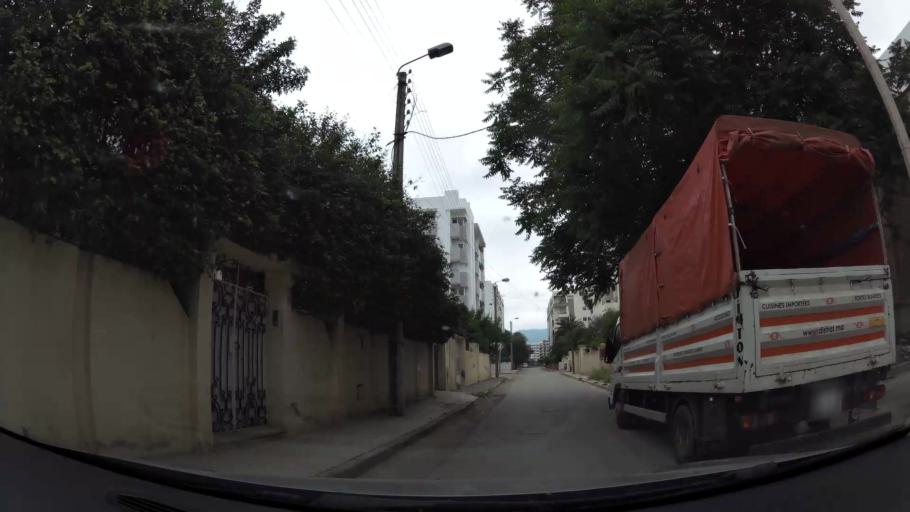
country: MA
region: Fes-Boulemane
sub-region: Fes
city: Fes
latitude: 34.0335
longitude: -5.0089
